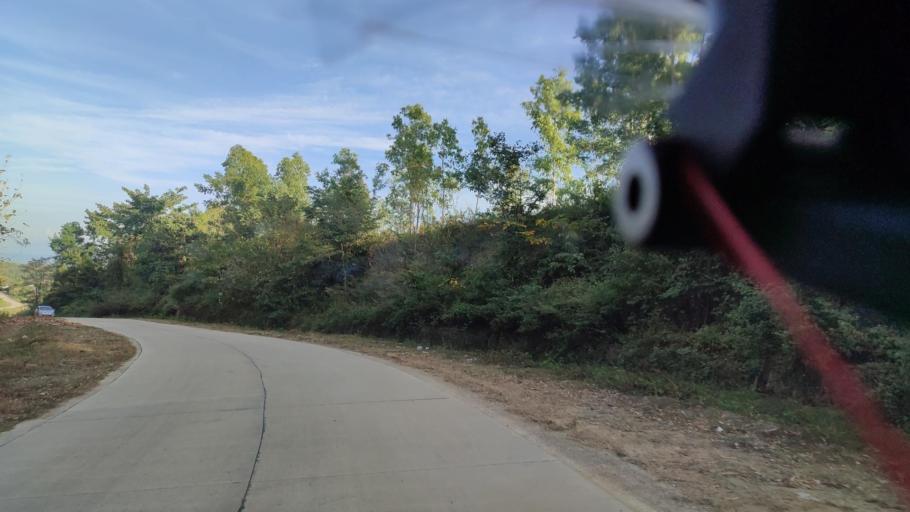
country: MM
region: Magway
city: Taungdwingyi
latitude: 20.0176
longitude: 95.7941
